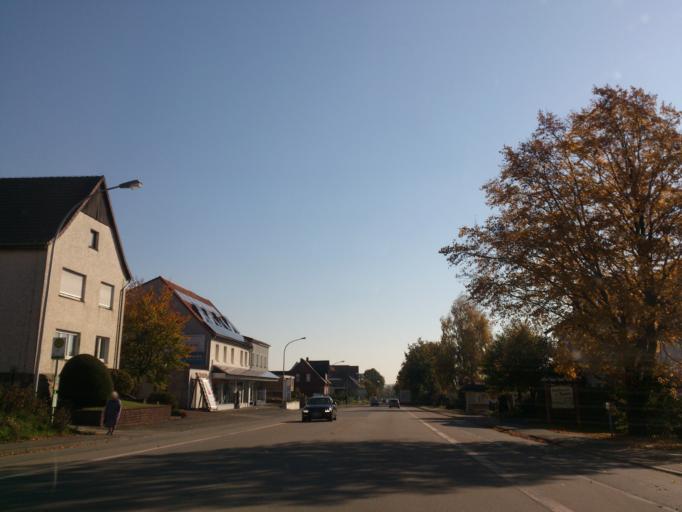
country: DE
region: North Rhine-Westphalia
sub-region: Regierungsbezirk Detmold
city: Willebadessen
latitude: 51.5286
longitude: 9.0375
